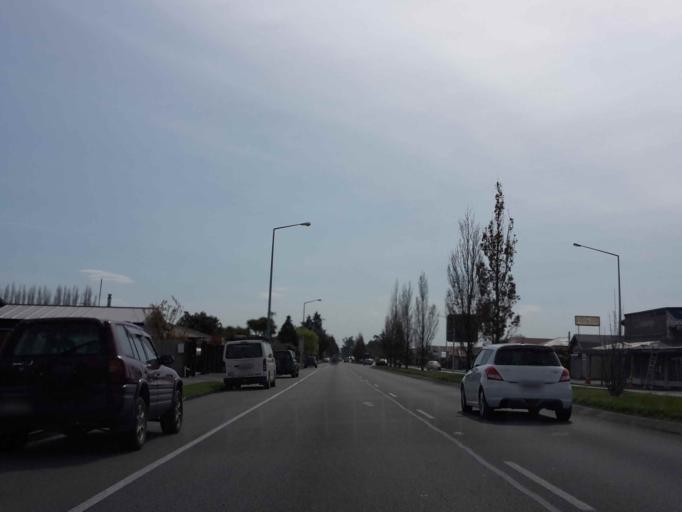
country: NZ
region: Canterbury
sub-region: Waimakariri District
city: Kaiapoi
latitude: -43.4483
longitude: 172.6302
